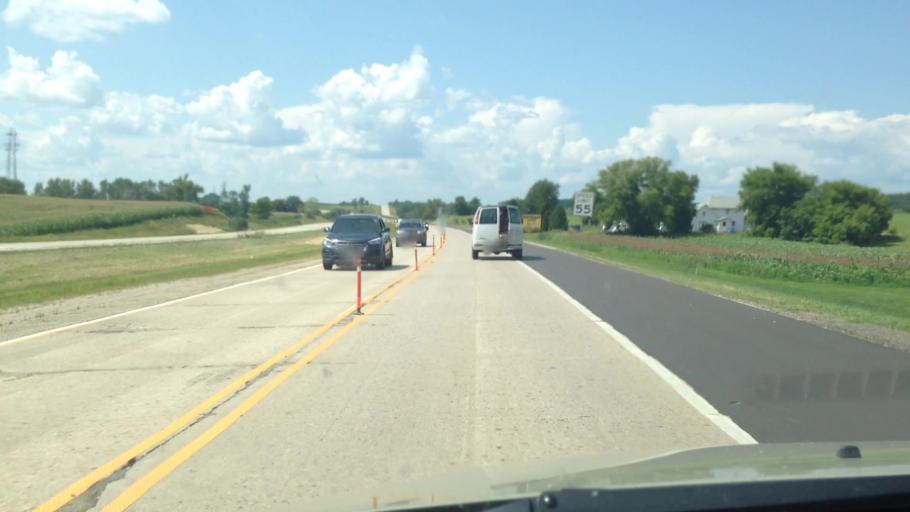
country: US
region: Wisconsin
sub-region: Shawano County
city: Bonduel
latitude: 44.7120
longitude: -88.3840
